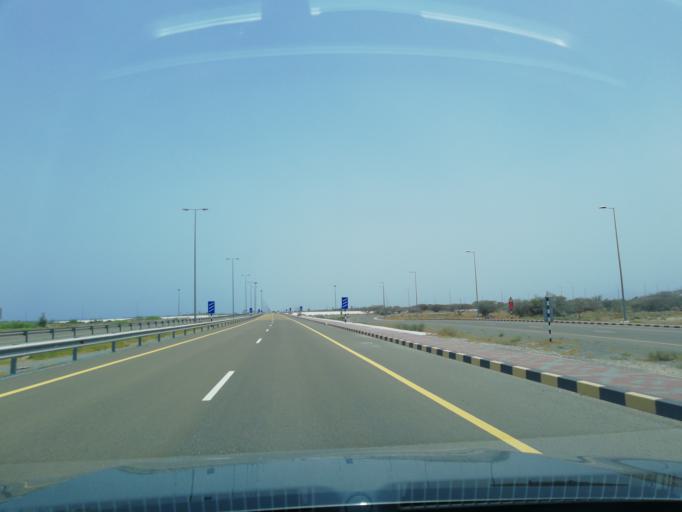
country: OM
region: Al Batinah
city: Shinas
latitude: 24.9210
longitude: 56.3869
